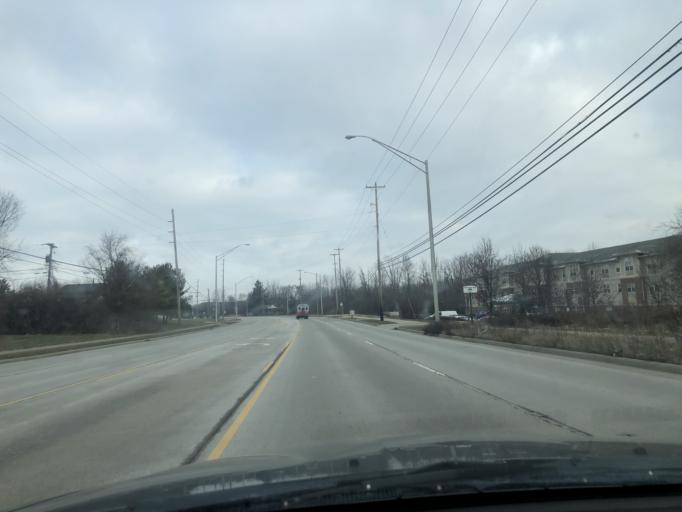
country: US
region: Ohio
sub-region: Franklin County
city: Obetz
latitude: 39.9101
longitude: -82.9284
